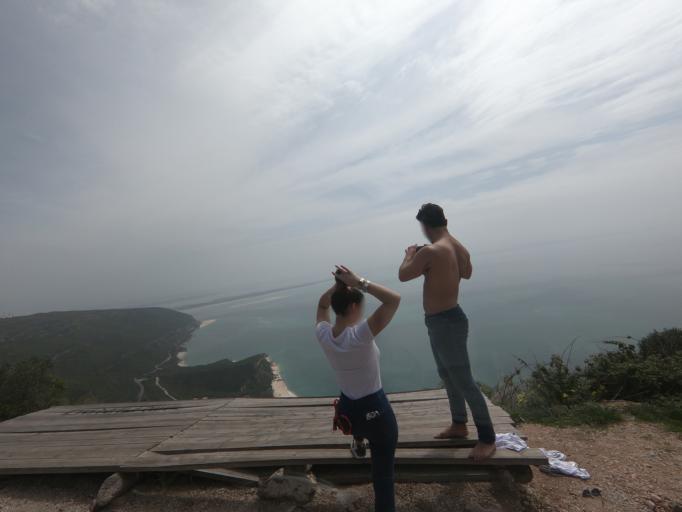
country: PT
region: Setubal
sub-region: Palmela
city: Quinta do Anjo
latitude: 38.4814
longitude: -8.9894
